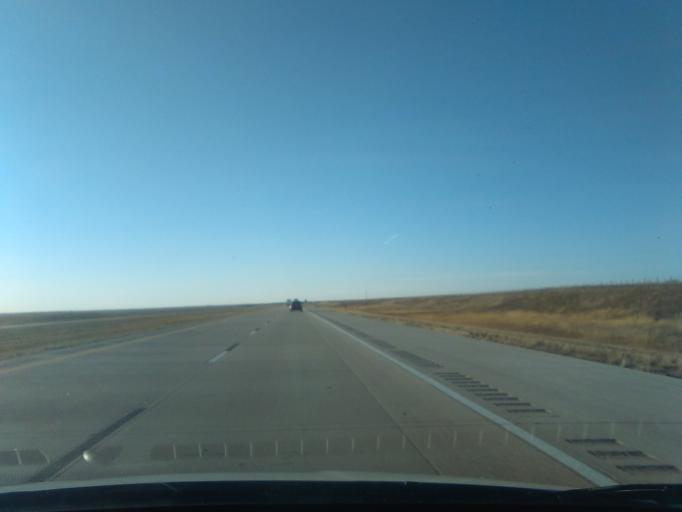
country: US
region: Nebraska
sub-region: Cheyenne County
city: Sidney
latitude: 41.1133
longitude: -102.7300
